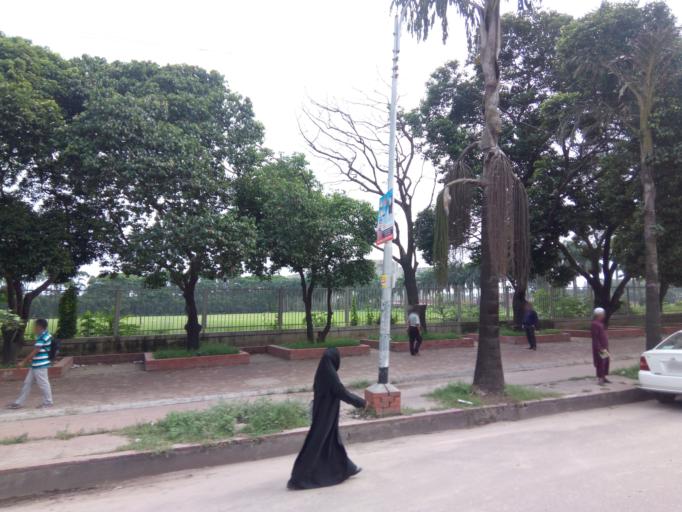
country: BD
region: Dhaka
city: Azimpur
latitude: 23.7584
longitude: 90.3764
